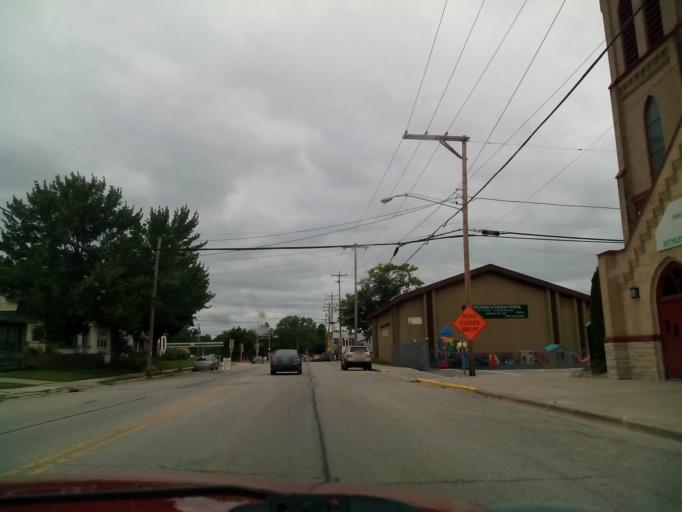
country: US
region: Wisconsin
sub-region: Outagamie County
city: Hortonville
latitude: 44.3361
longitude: -88.6378
